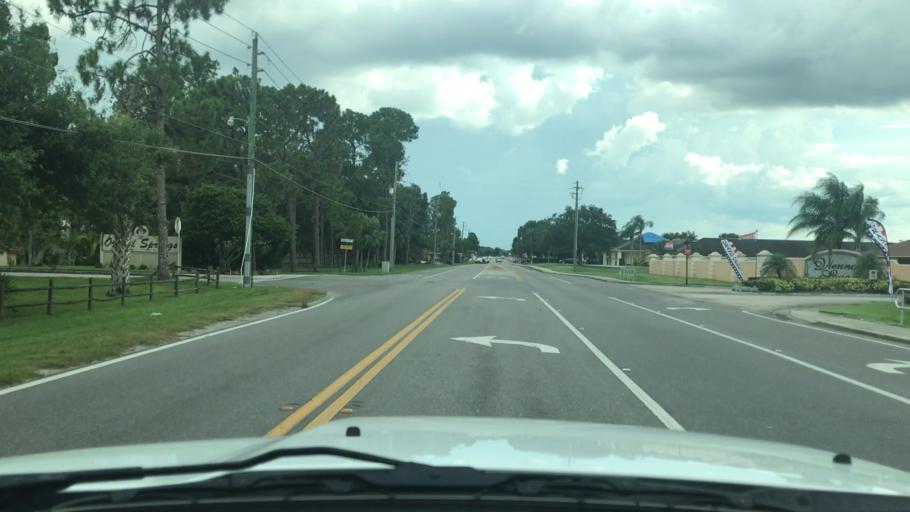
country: US
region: Florida
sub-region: Polk County
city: Cypress Gardens
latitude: 28.0122
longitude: -81.6792
